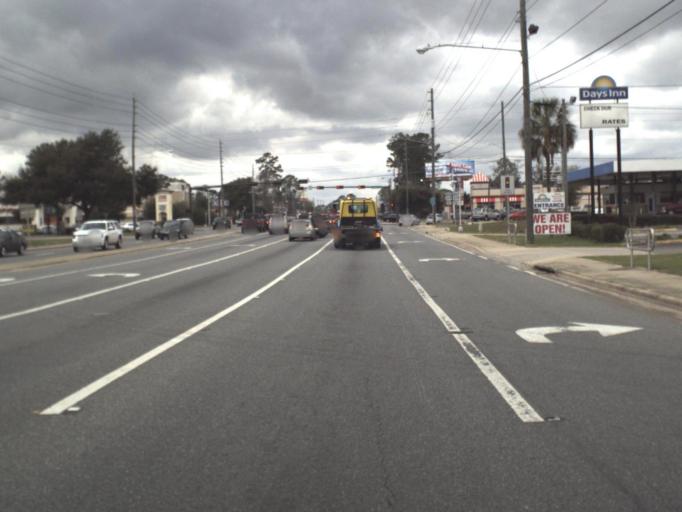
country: US
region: Florida
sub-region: Leon County
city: Tallahassee
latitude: 30.4276
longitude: -84.2252
